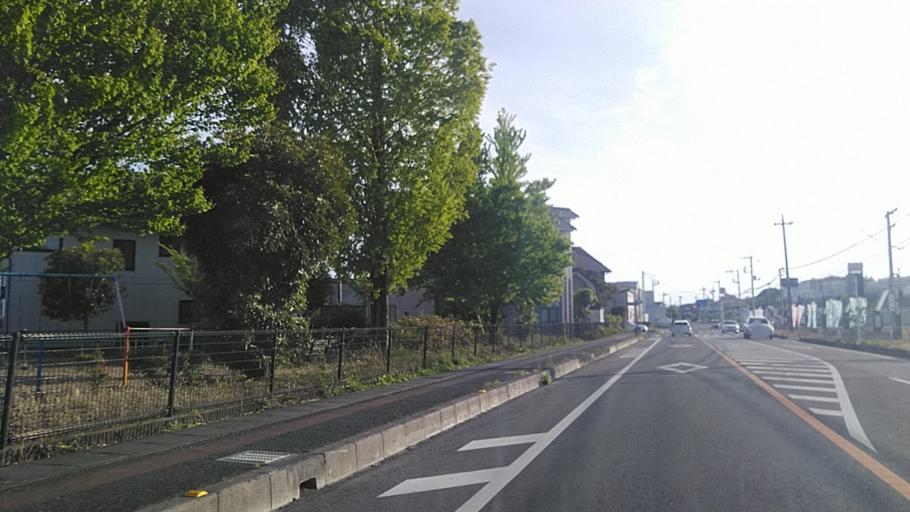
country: JP
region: Gunma
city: Ota
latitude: 36.3088
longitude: 139.3882
